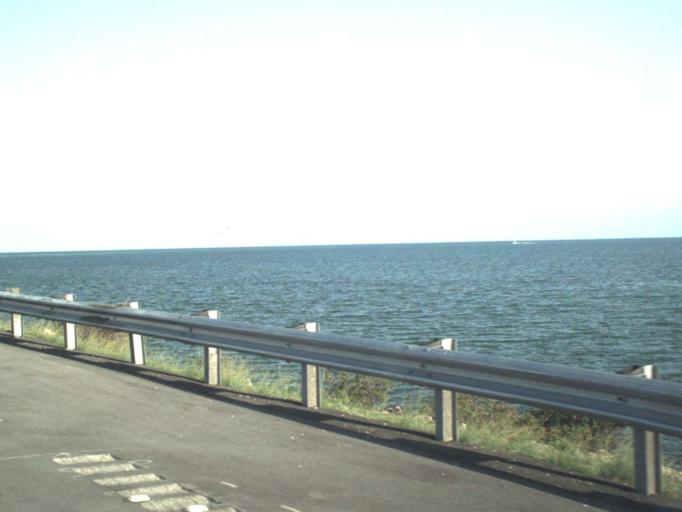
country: US
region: Florida
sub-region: Monroe County
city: Islamorada
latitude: 24.8397
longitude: -80.7809
